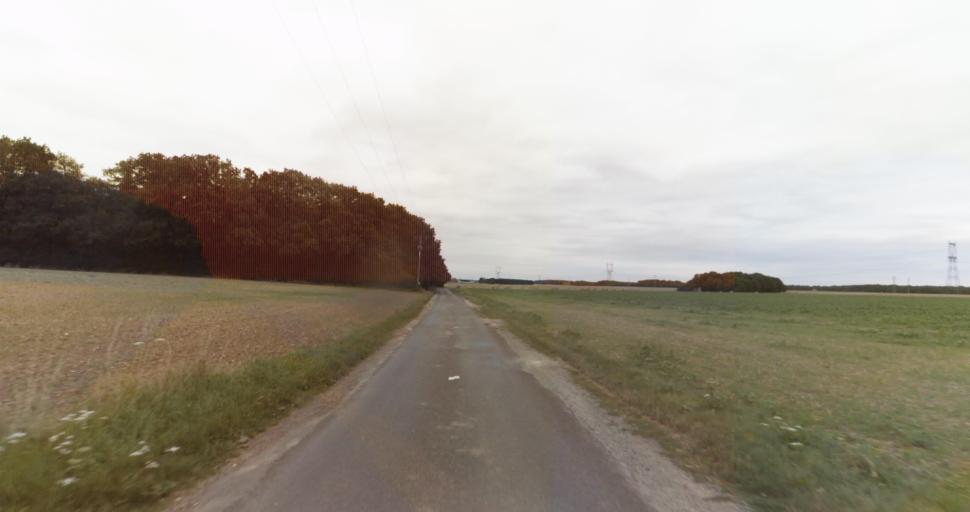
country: FR
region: Haute-Normandie
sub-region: Departement de l'Eure
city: Marcilly-sur-Eure
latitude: 48.8640
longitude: 1.2815
